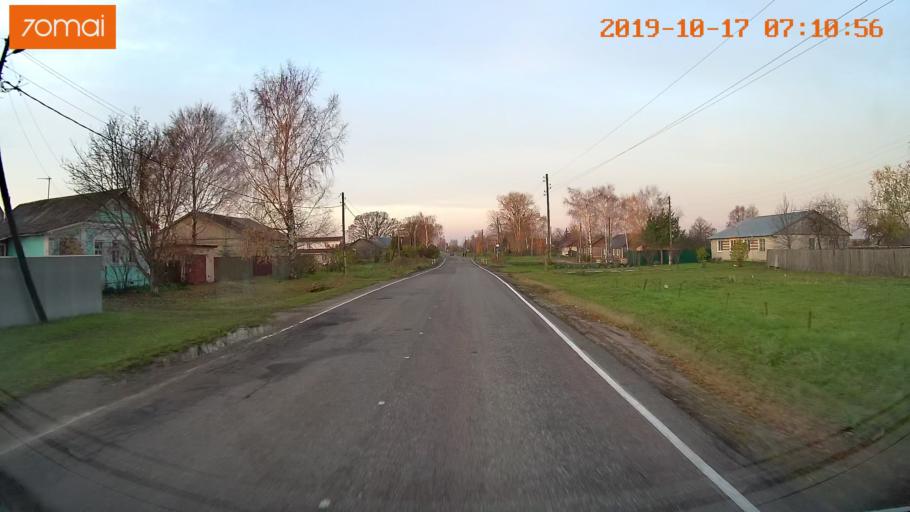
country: RU
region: Vladimir
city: Suzdal'
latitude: 56.4082
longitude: 40.3508
